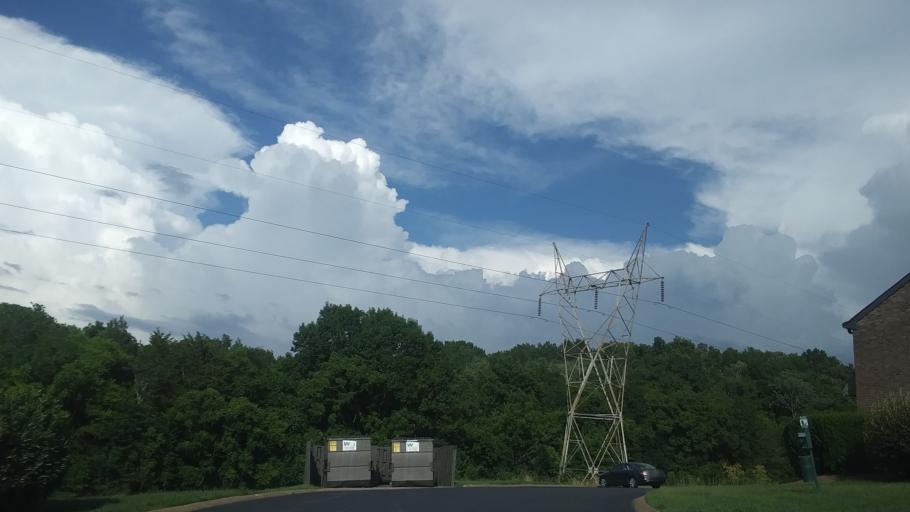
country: US
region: Tennessee
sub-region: Rutherford County
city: La Vergne
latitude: 36.0849
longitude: -86.6416
